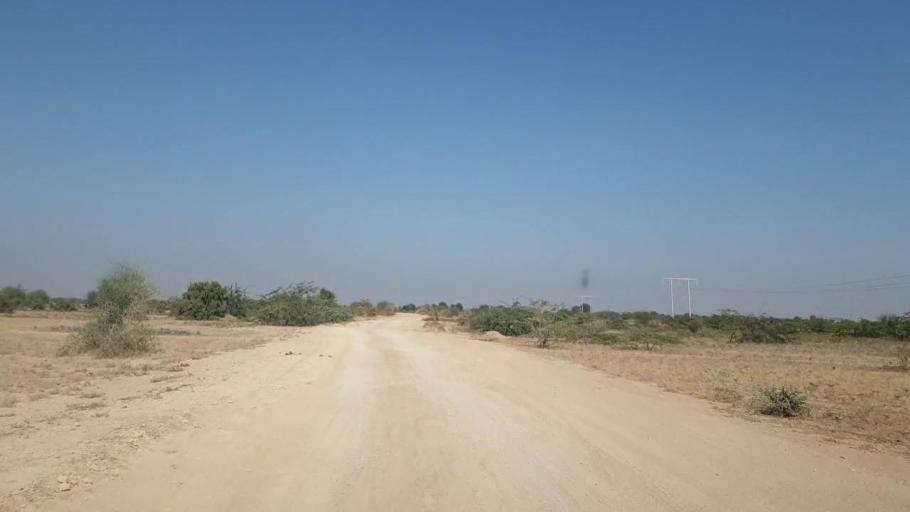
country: PK
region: Sindh
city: Jamshoro
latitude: 25.3125
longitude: 67.8188
